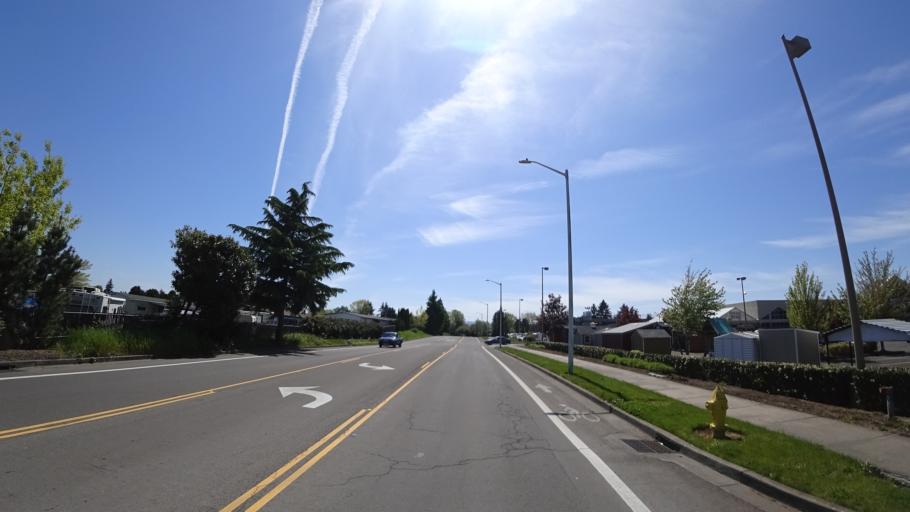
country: US
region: Oregon
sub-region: Washington County
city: Hillsboro
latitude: 45.5037
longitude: -122.9560
